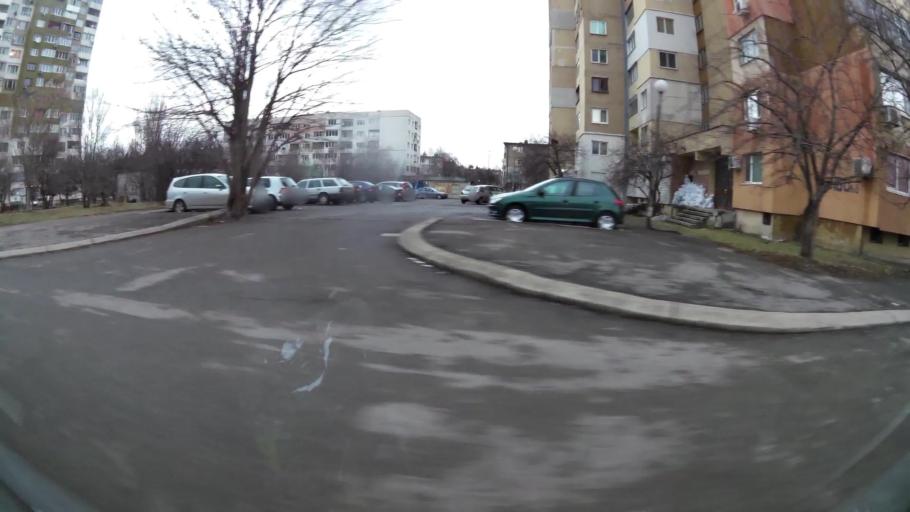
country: BG
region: Sofia-Capital
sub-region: Stolichna Obshtina
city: Sofia
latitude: 42.7356
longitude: 23.2970
